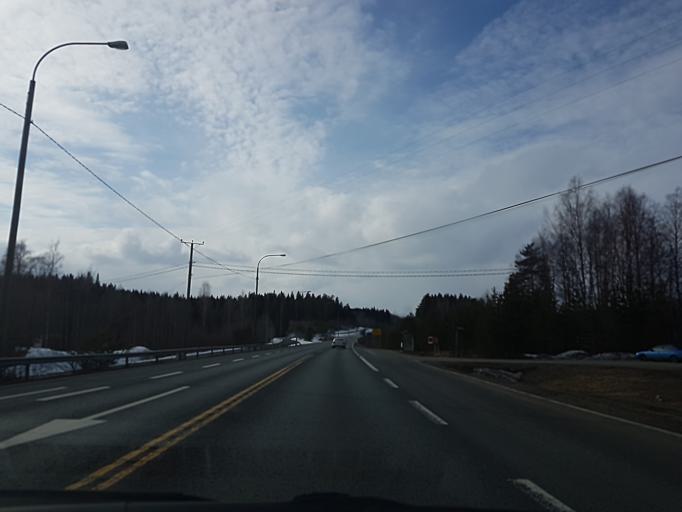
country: FI
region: Northern Savo
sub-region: Kuopio
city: Vehmersalmi
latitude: 62.9388
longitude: 27.9137
